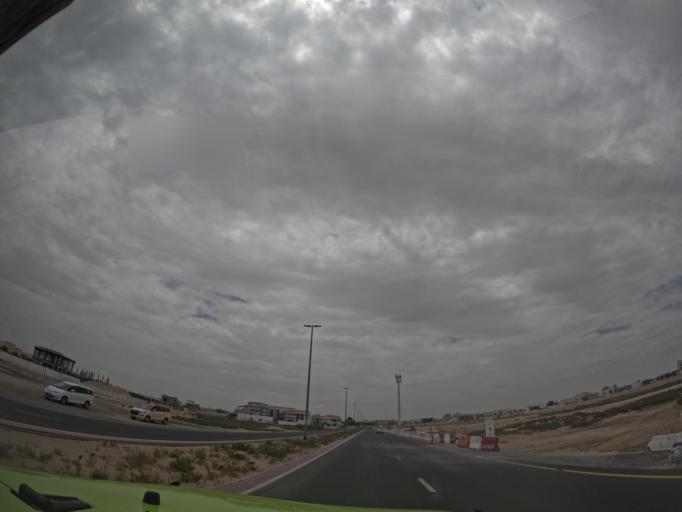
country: AE
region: Ash Shariqah
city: Sharjah
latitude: 25.1563
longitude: 55.3724
